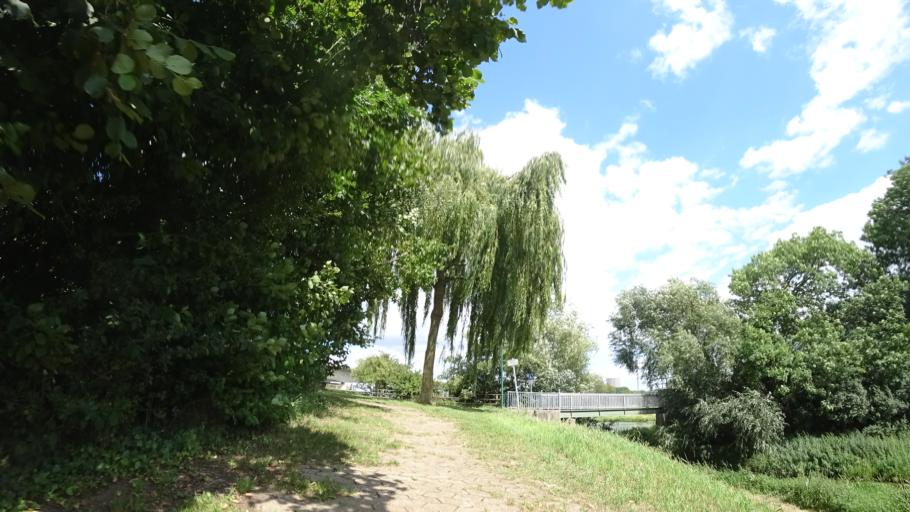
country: DE
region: North Rhine-Westphalia
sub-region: Regierungsbezirk Detmold
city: Petershagen
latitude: 52.3805
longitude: 8.9711
